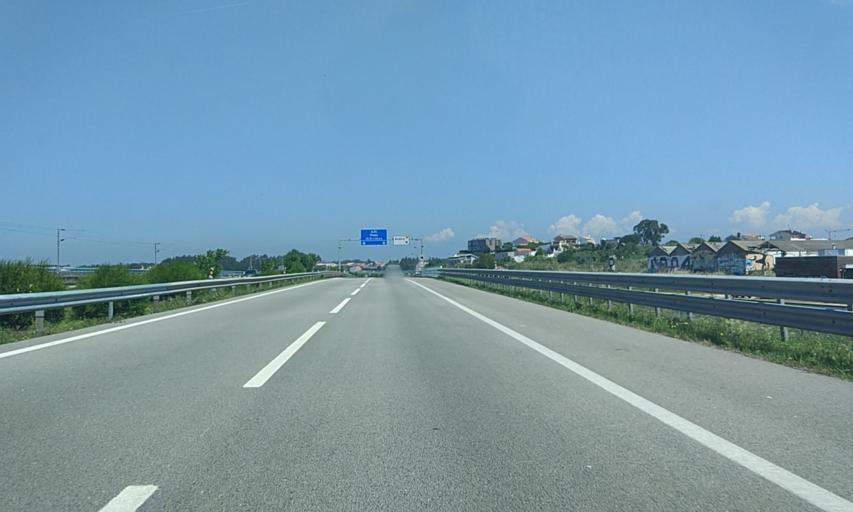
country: PT
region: Aveiro
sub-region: Aveiro
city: Aveiro
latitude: 40.6503
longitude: -8.6454
